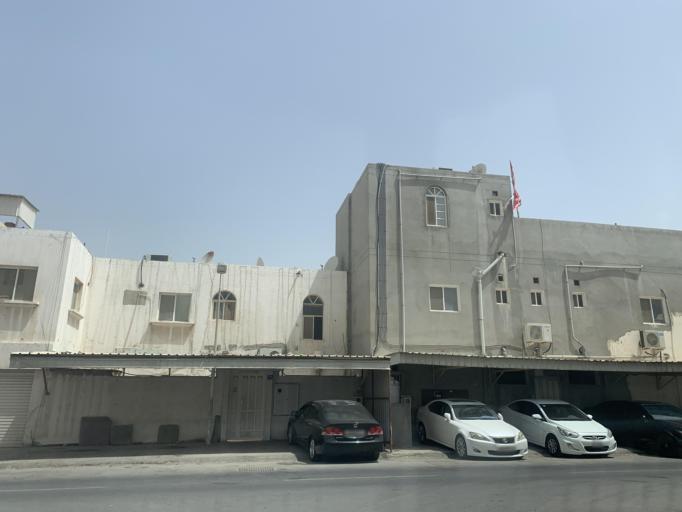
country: BH
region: Northern
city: Madinat `Isa
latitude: 26.1493
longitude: 50.5255
